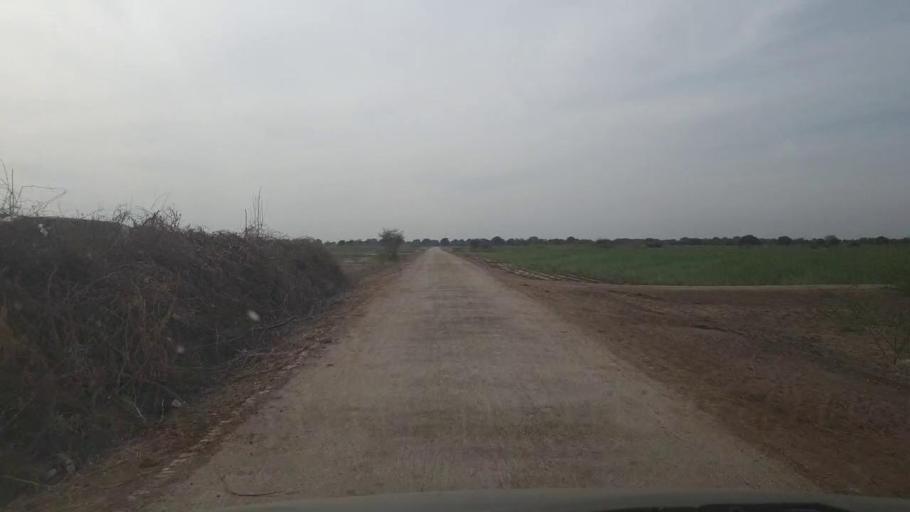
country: PK
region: Sindh
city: Kunri
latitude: 25.2818
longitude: 69.5919
